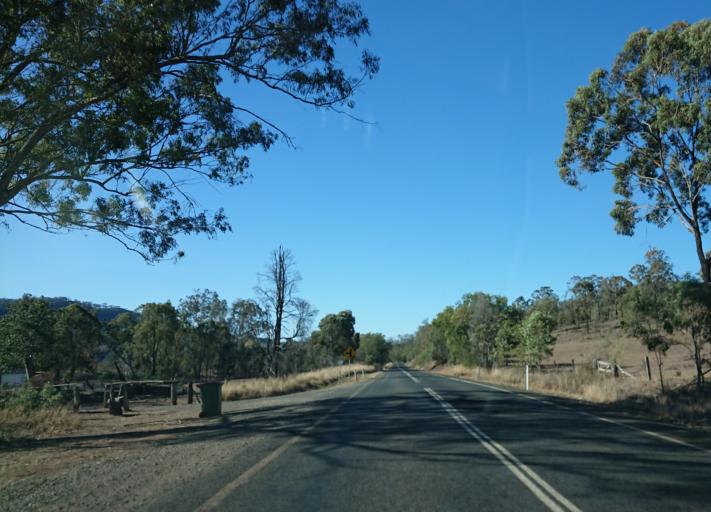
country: AU
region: Queensland
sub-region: Toowoomba
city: Top Camp
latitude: -27.7312
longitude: 152.1111
